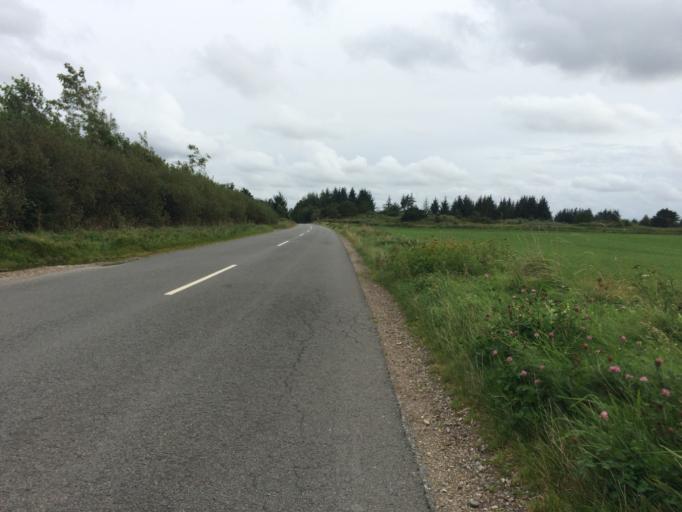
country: DK
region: Central Jutland
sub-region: Holstebro Kommune
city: Ulfborg
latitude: 56.2254
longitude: 8.3842
